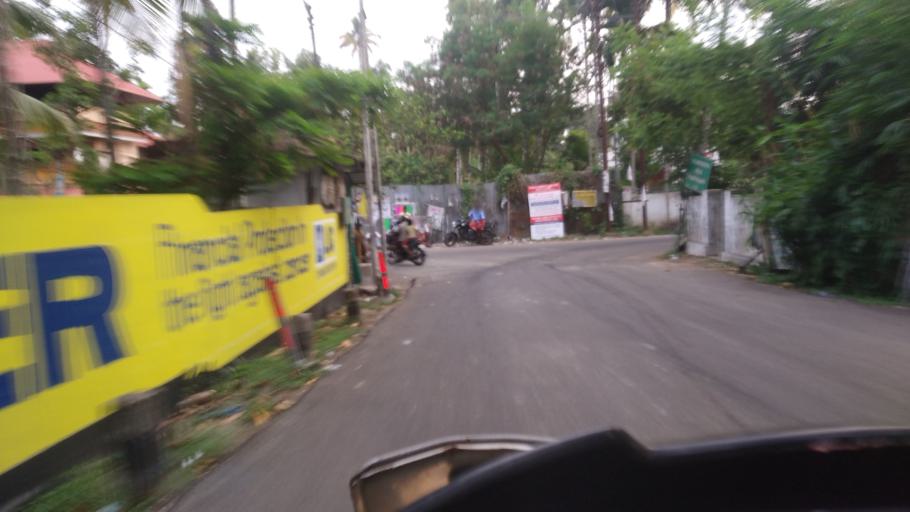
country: IN
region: Kerala
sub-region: Thrissur District
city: Kodungallur
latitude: 10.1671
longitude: 76.1982
